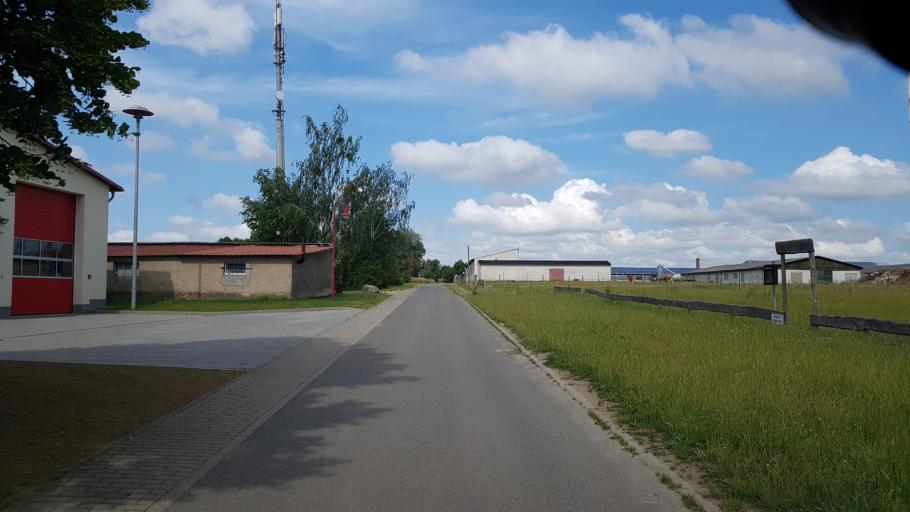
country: DE
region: Mecklenburg-Vorpommern
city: Strasburg
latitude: 53.4366
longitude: 13.7075
